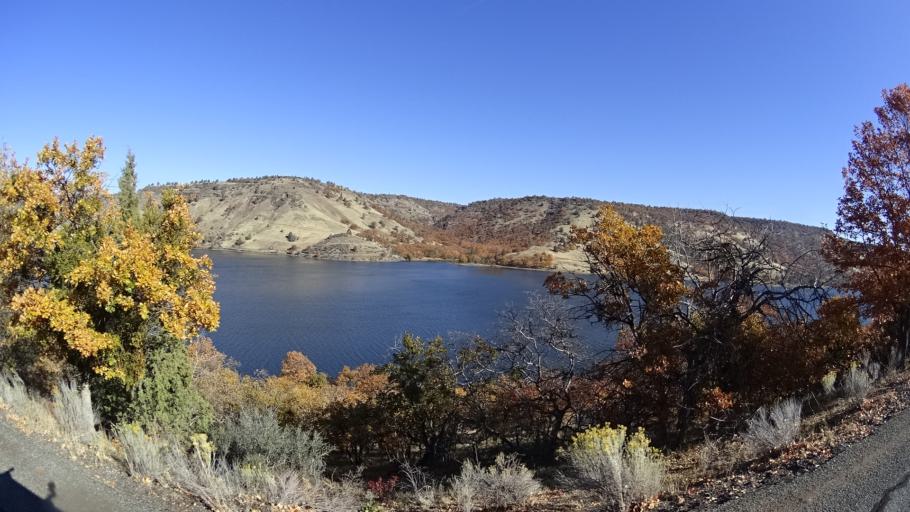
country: US
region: California
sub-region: Siskiyou County
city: Montague
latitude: 41.9772
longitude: -122.3044
